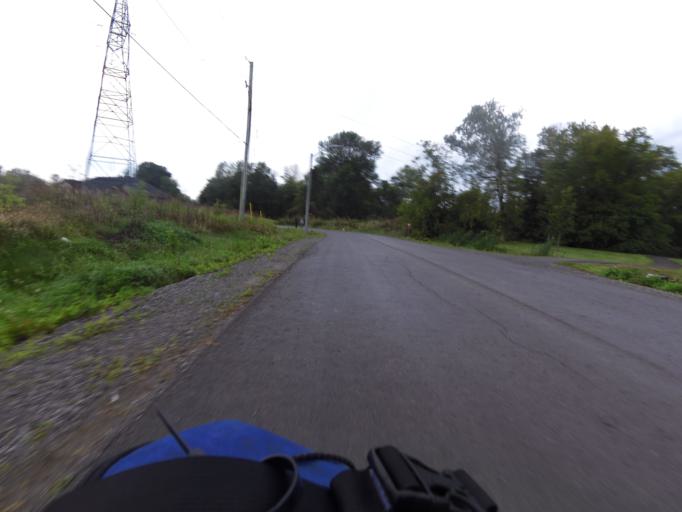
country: CA
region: Ontario
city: Ottawa
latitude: 45.2290
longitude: -75.4740
